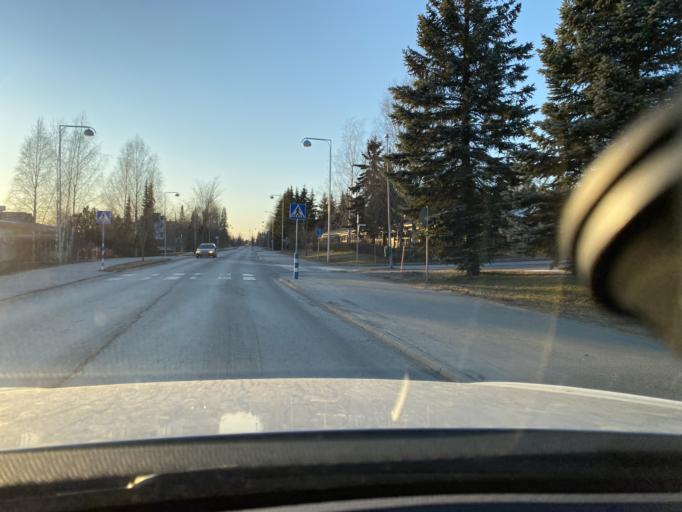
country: FI
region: Pirkanmaa
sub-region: Lounais-Pirkanmaa
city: Punkalaidun
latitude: 61.1127
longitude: 23.1025
